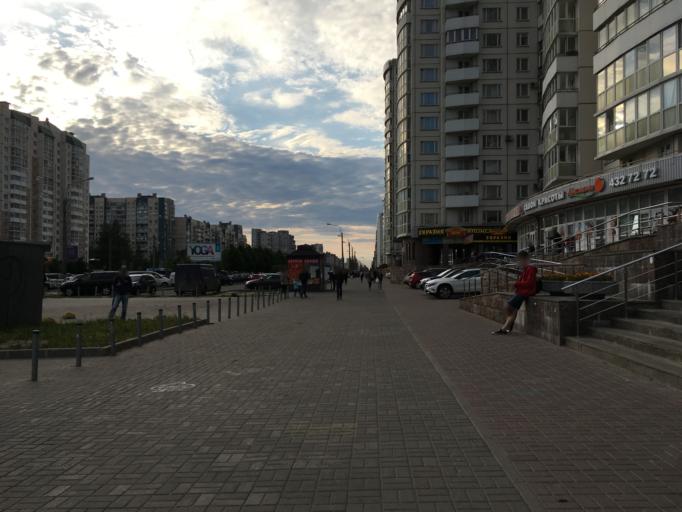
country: RU
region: St.-Petersburg
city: Komendantsky aerodrom
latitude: 60.0089
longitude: 30.2592
